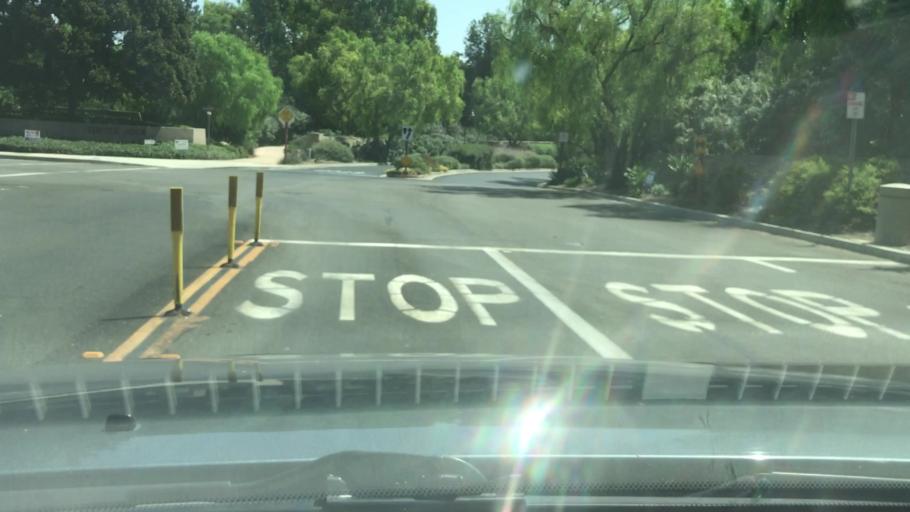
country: US
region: California
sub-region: Orange County
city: San Joaquin Hills
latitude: 33.6327
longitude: -117.8030
